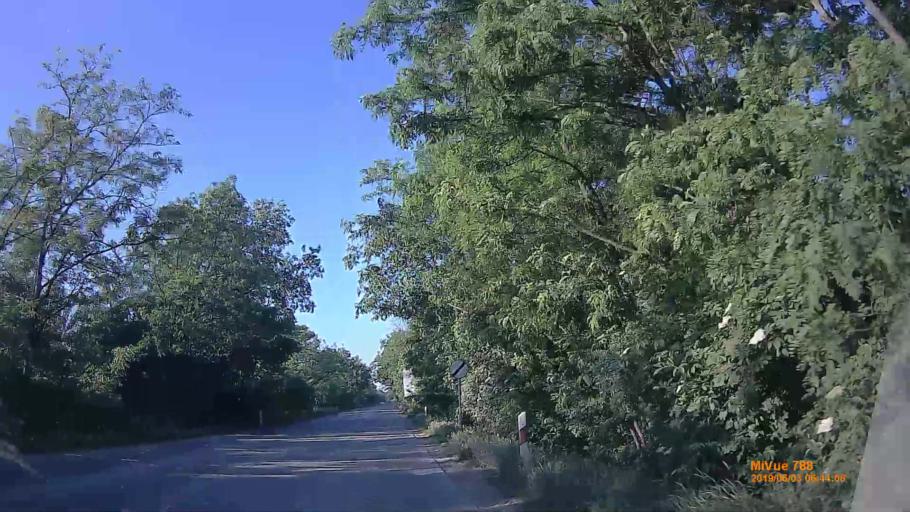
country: HU
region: Pest
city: Bugyi
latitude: 47.2477
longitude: 19.1291
